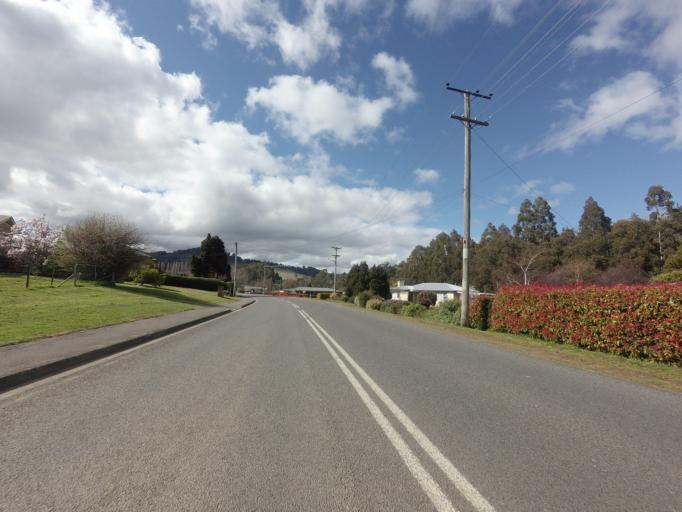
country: AU
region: Tasmania
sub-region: Huon Valley
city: Geeveston
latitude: -43.1704
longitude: 146.9254
